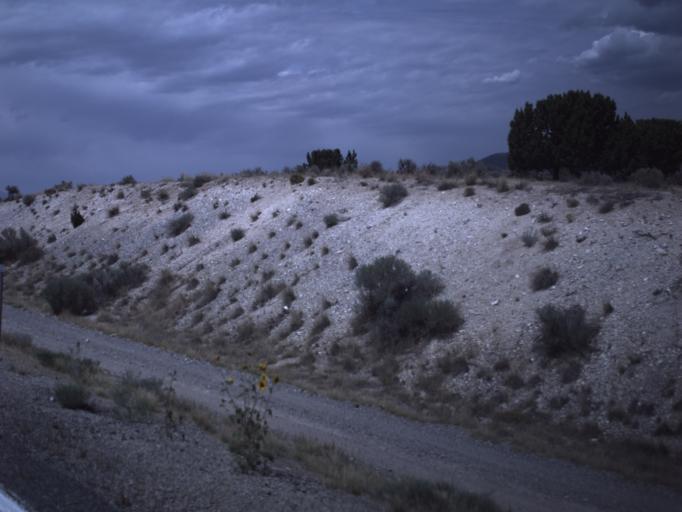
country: US
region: Utah
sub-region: Utah County
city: Eagle Mountain
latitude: 40.2319
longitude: -112.1908
